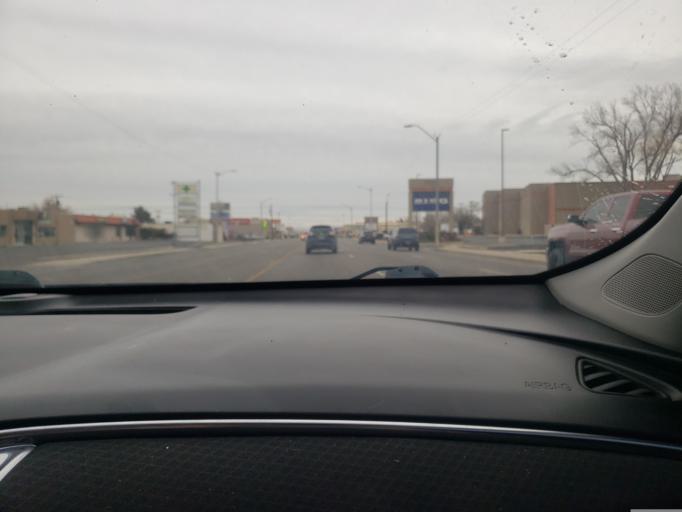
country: US
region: New Mexico
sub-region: Bernalillo County
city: Albuquerque
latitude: 35.1114
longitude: -106.5863
